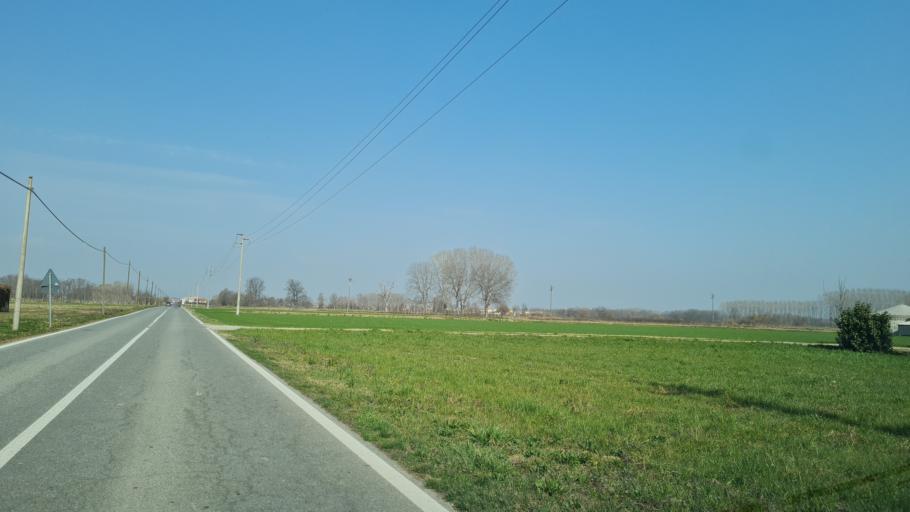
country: IT
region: Piedmont
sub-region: Provincia di Novara
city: Carpignano Sesia
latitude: 45.5180
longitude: 8.4192
